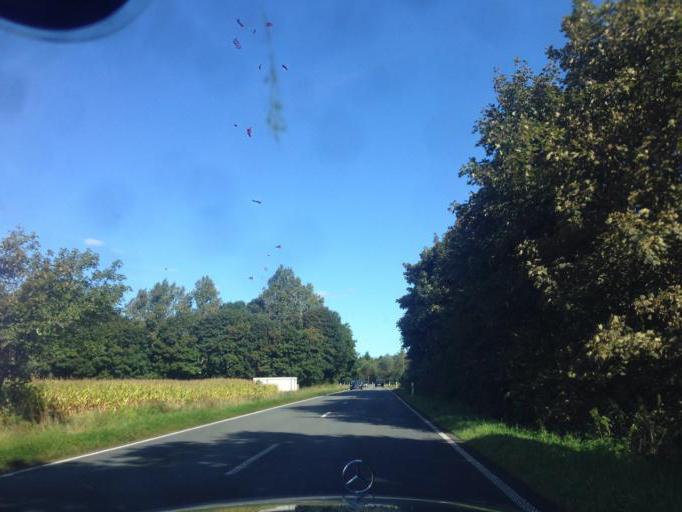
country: DE
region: Schleswig-Holstein
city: Nordhackstedt
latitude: 54.7590
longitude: 9.1529
